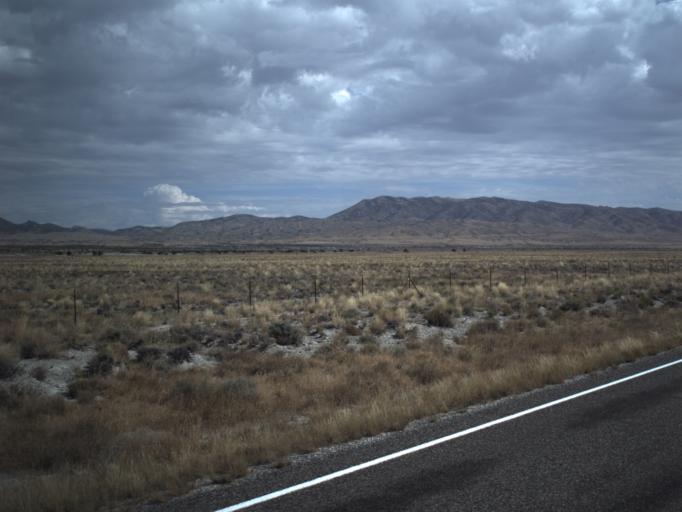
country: US
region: Utah
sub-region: Tooele County
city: Wendover
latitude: 41.4306
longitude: -113.8032
